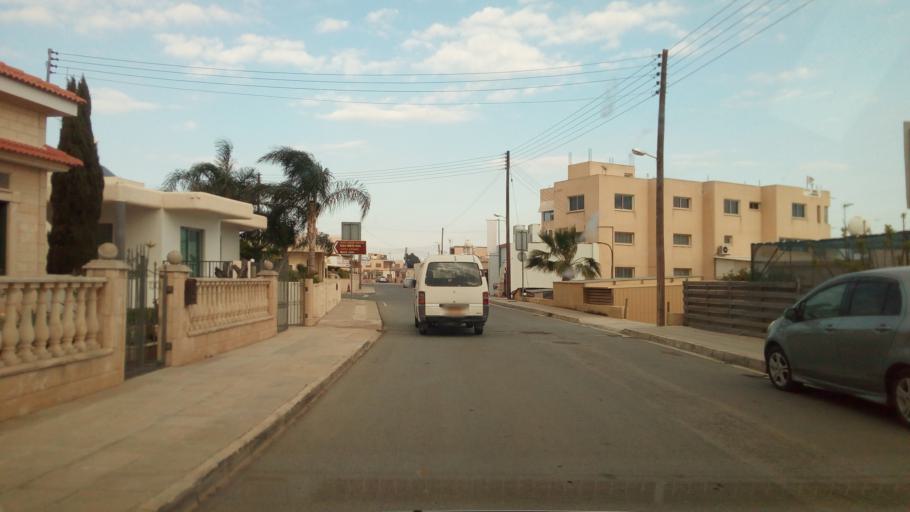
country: CY
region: Larnaka
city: Xylotymbou
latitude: 35.0130
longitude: 33.7368
